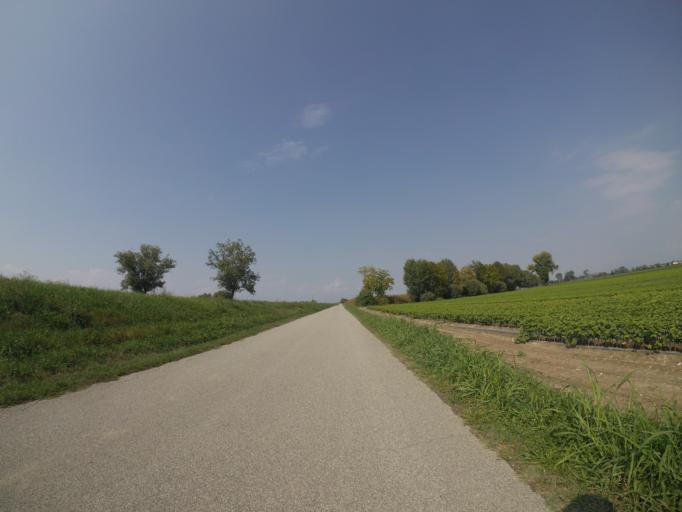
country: IT
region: Friuli Venezia Giulia
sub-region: Provincia di Udine
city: Camino al Tagliamento
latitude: 45.9207
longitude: 12.9256
